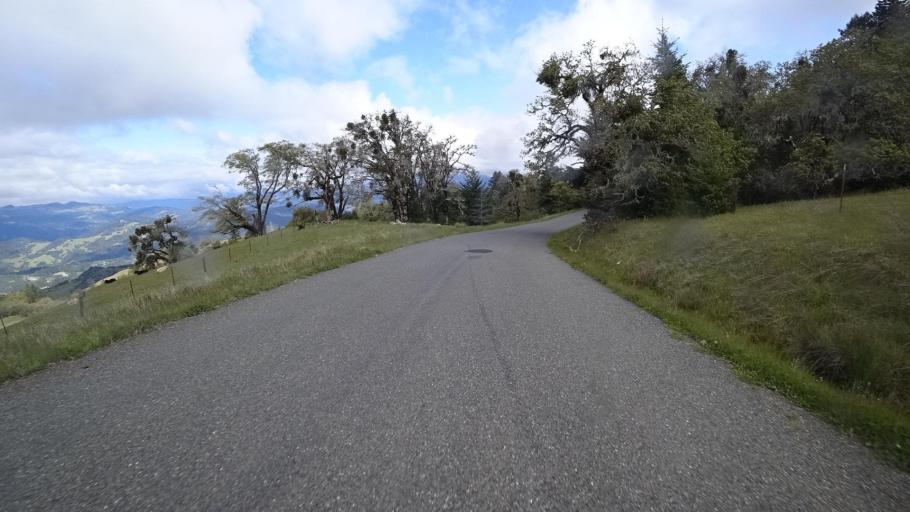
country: US
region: California
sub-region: Humboldt County
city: Redway
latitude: 40.1553
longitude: -123.5588
